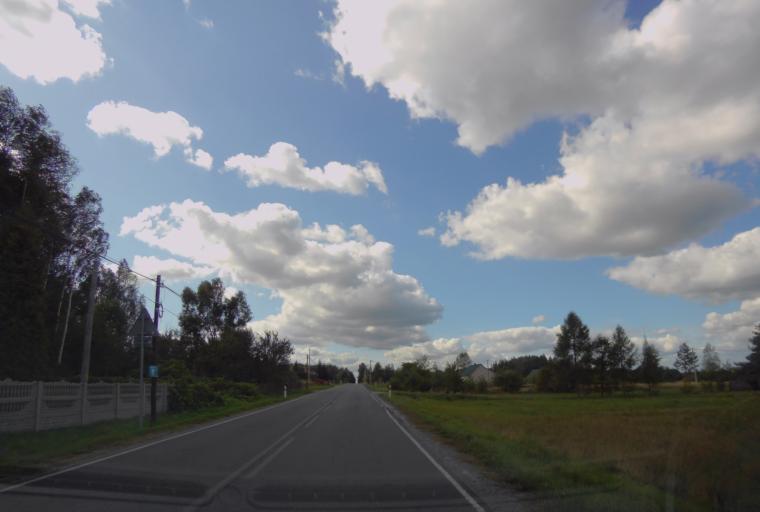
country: PL
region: Subcarpathian Voivodeship
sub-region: Powiat tarnobrzeski
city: Nowa Deba
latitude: 50.4045
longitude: 21.8072
